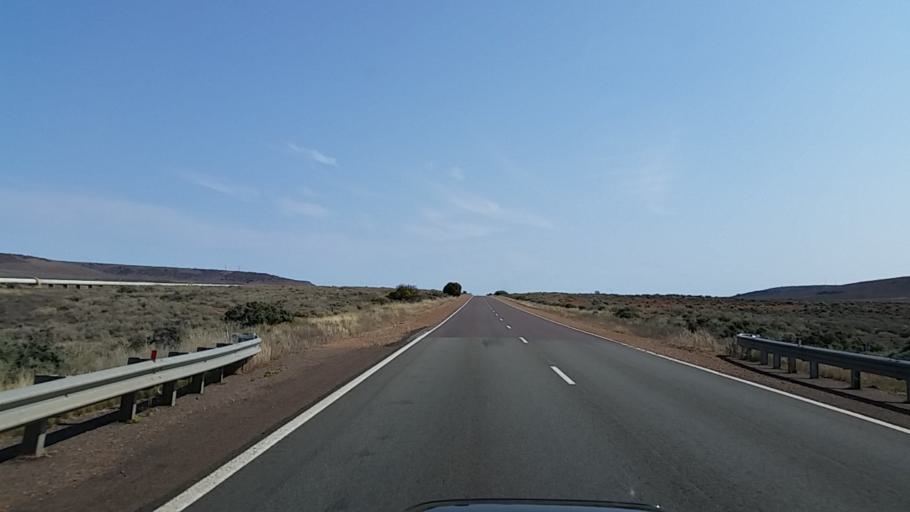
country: AU
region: South Australia
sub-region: Port Augusta
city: Port Augusta West
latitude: -32.5879
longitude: 137.6124
